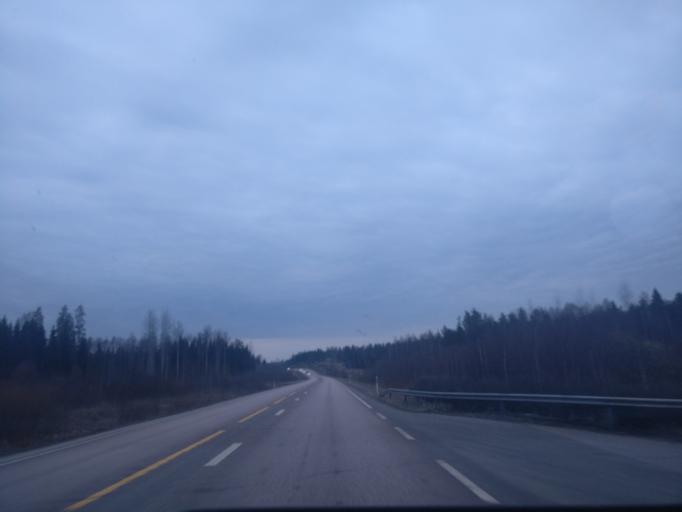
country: FI
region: Paijanne Tavastia
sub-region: Lahti
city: Heinola
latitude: 61.3404
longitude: 26.0426
